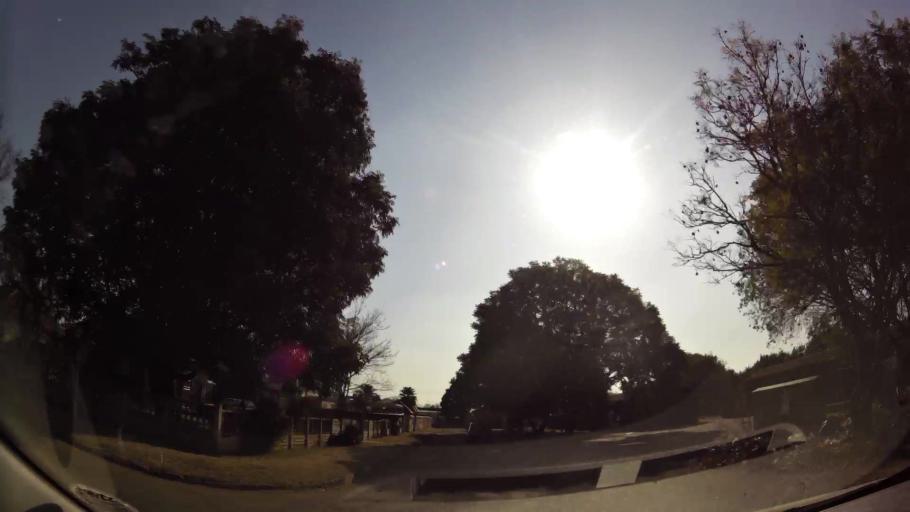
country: ZA
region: Gauteng
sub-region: West Rand District Municipality
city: Randfontein
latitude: -26.1713
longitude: 27.7094
